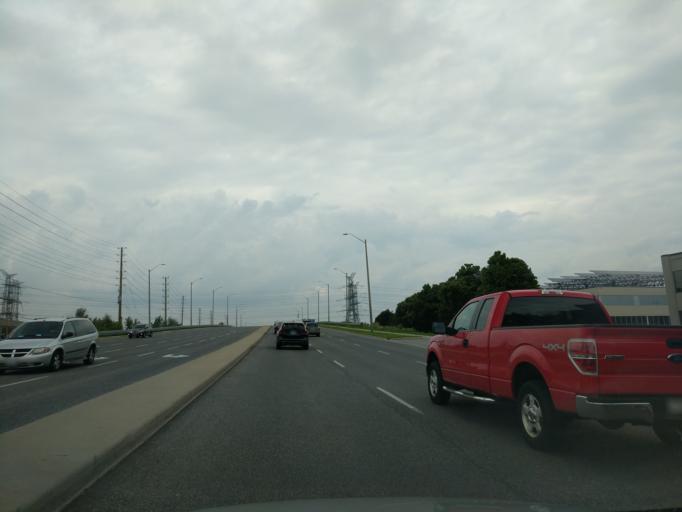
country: CA
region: Ontario
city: Markham
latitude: 43.8384
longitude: -79.3293
